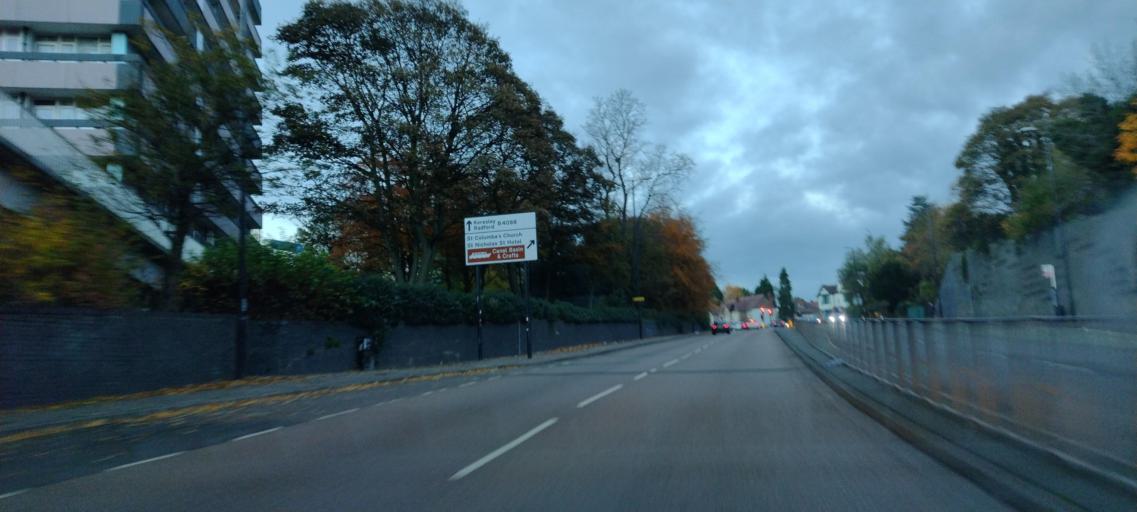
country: GB
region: England
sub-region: Coventry
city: Coventry
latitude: 52.4131
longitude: -1.5151
